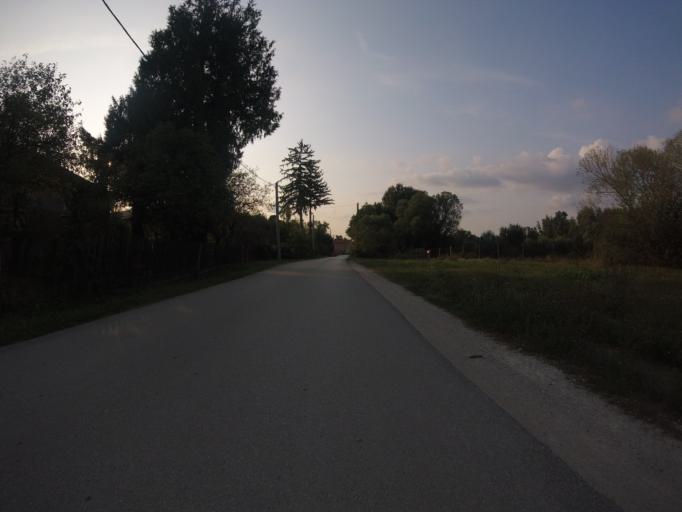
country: HR
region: Zagrebacka
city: Kuce
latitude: 45.7293
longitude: 16.1980
